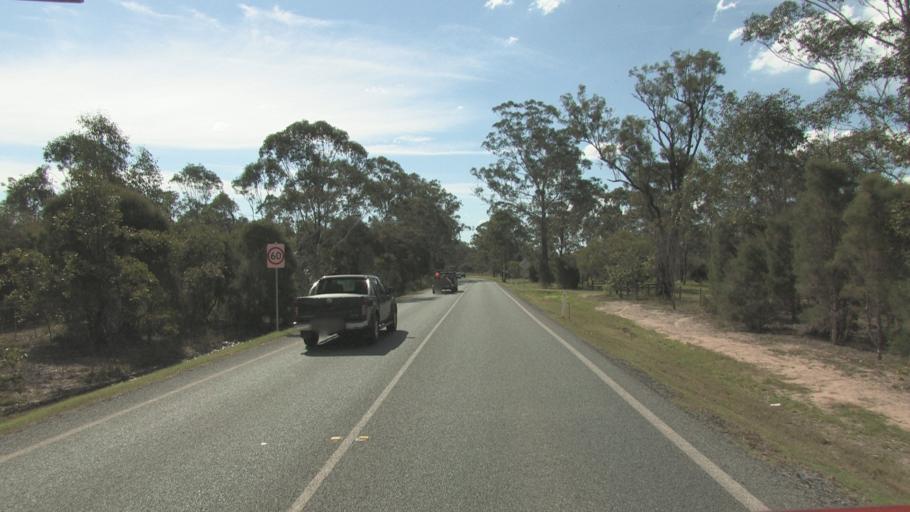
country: AU
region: Queensland
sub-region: Logan
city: Cedar Vale
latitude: -27.8297
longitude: 153.0392
